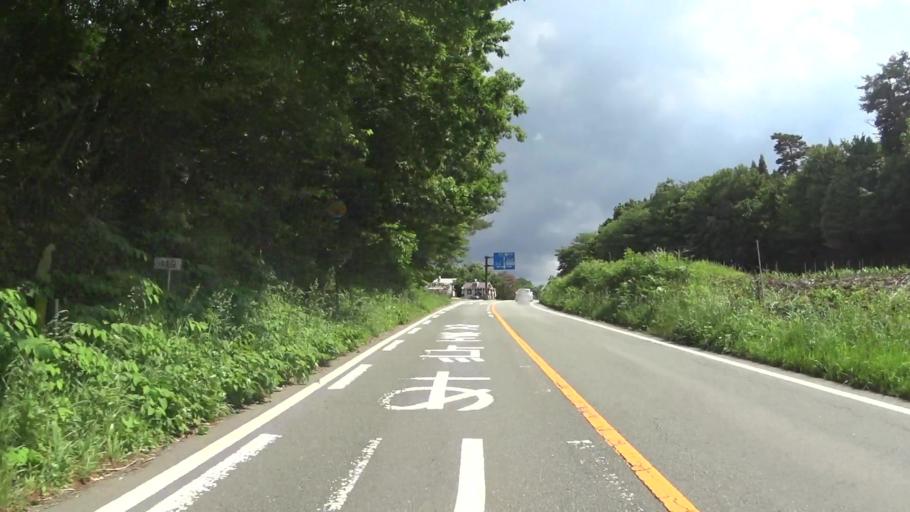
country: JP
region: Kumamoto
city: Aso
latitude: 33.0374
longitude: 131.1650
